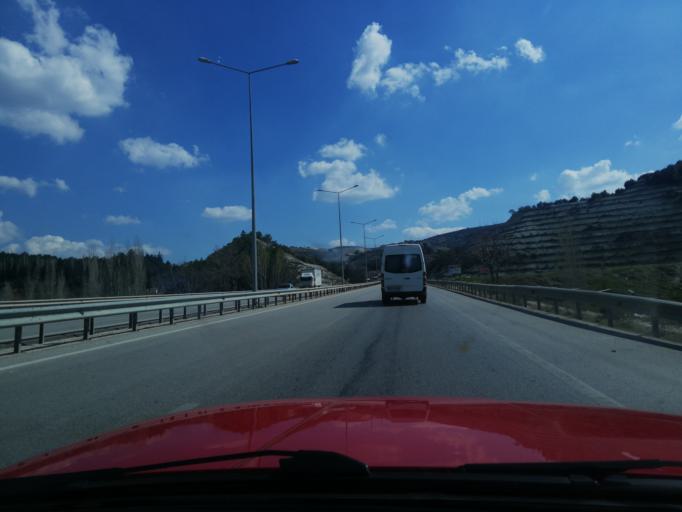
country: TR
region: Burdur
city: Burdur
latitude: 37.7061
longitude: 30.3059
